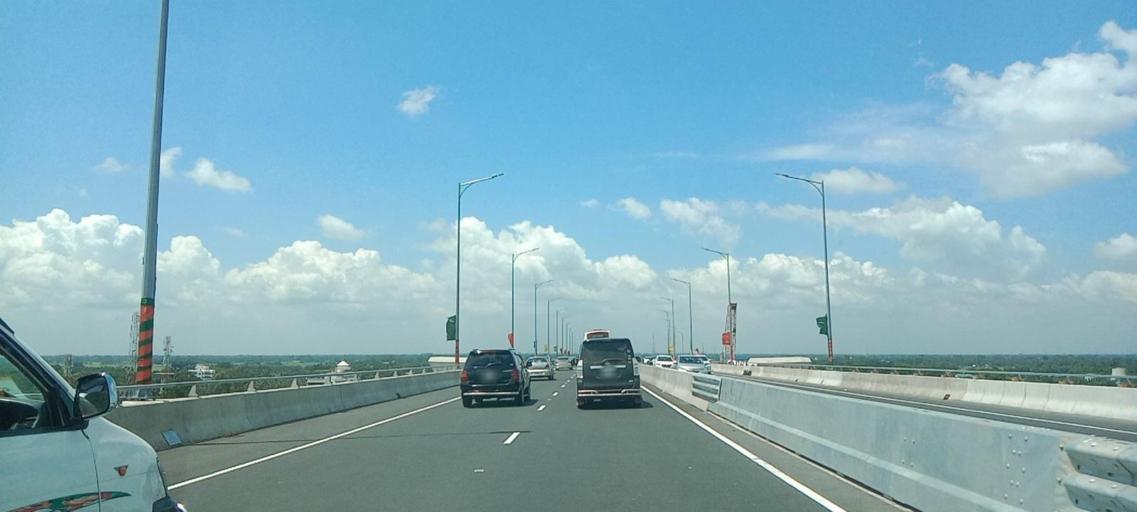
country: BD
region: Dhaka
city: Char Bhadrasan
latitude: 23.4698
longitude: 90.2643
